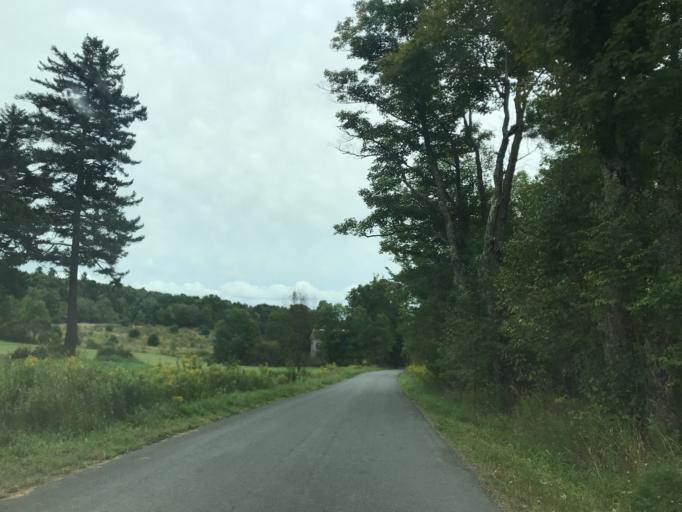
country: US
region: New York
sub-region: Otsego County
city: Worcester
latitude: 42.5787
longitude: -74.6720
